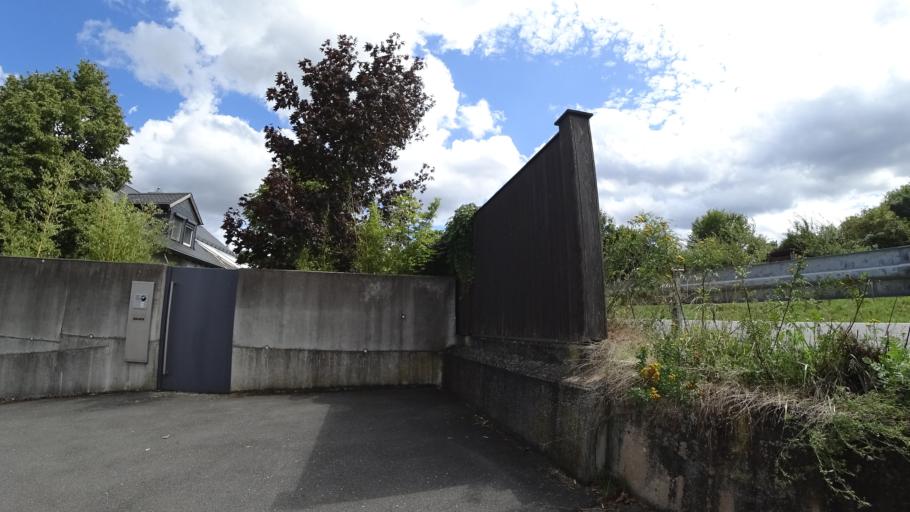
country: DE
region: Bavaria
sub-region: Regierungsbezirk Unterfranken
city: Miltenberg
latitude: 49.7023
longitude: 9.2778
